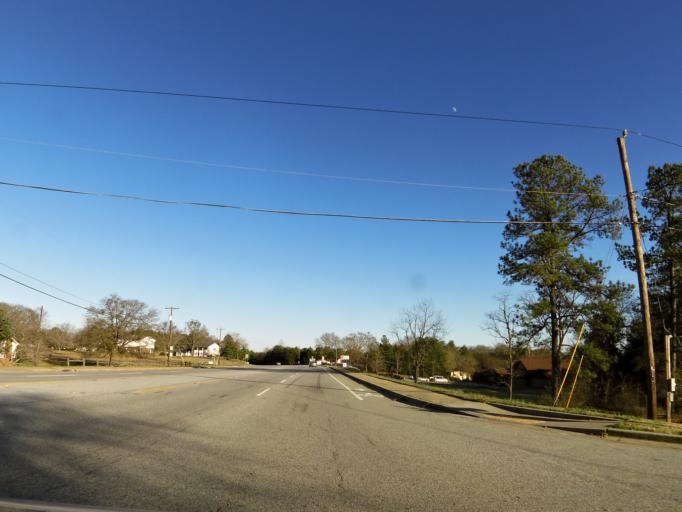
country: US
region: South Carolina
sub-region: Spartanburg County
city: Fairforest
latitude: 34.8897
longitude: -82.0507
